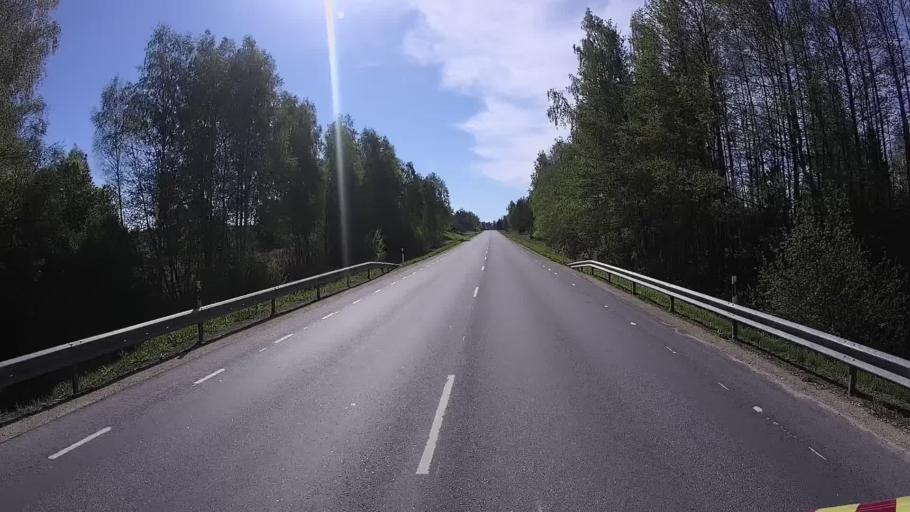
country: EE
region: Tartu
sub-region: UElenurme vald
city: Ulenurme
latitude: 58.3458
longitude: 26.9427
